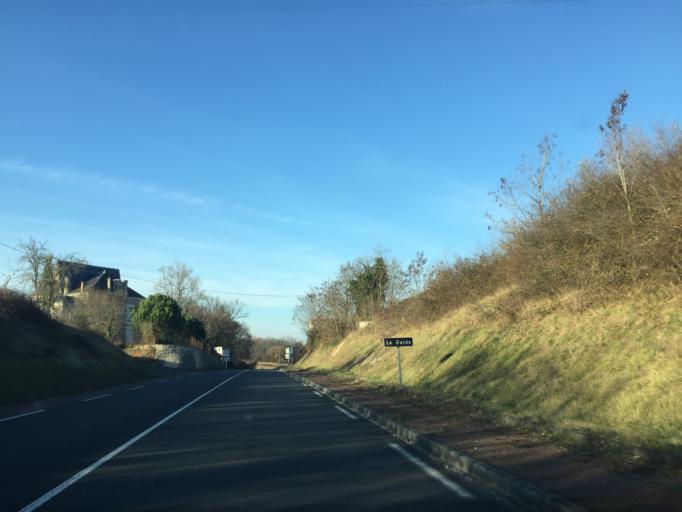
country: FR
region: Aquitaine
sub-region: Departement de la Dordogne
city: Riberac
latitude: 45.1985
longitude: 0.3680
